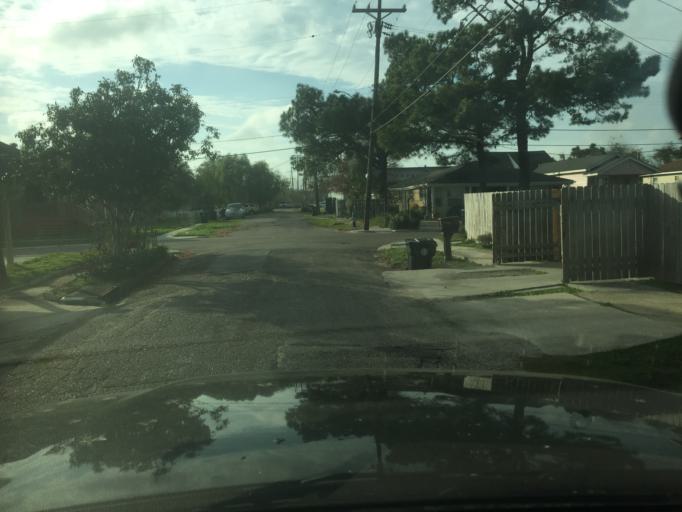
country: US
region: Louisiana
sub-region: Orleans Parish
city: New Orleans
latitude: 29.9936
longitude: -90.0813
